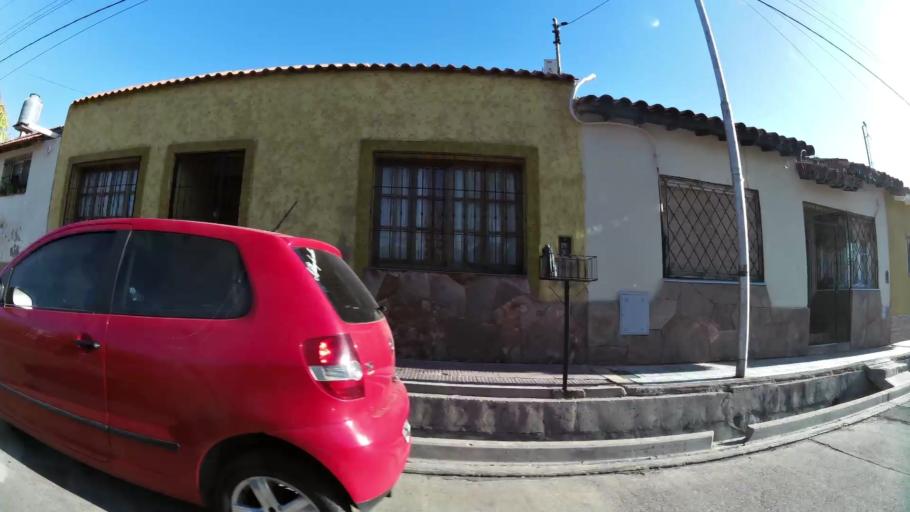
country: AR
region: Mendoza
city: Las Heras
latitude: -32.8619
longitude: -68.8322
